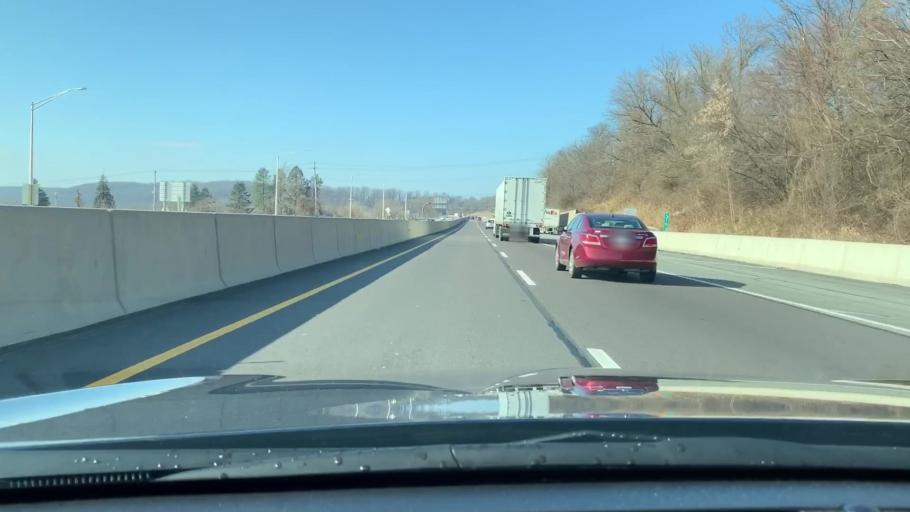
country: US
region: Pennsylvania
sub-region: Chester County
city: Malvern
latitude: 40.0756
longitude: -75.5335
